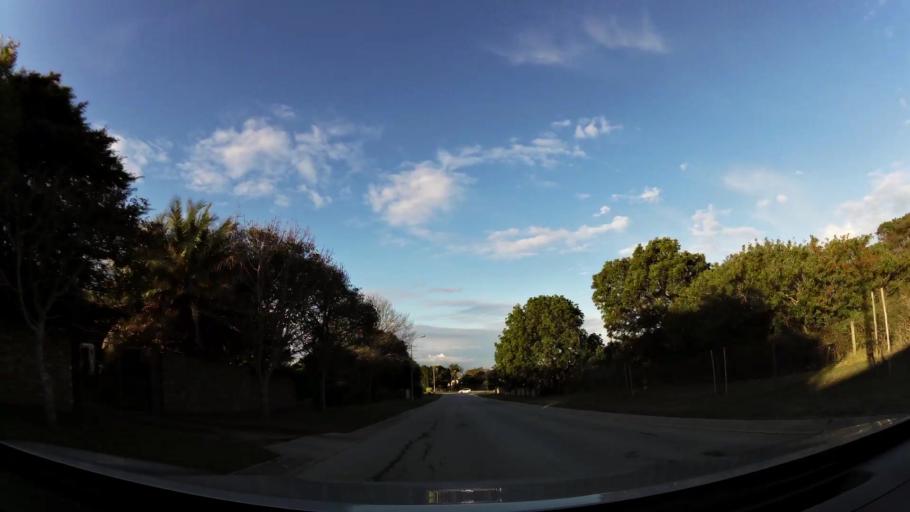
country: ZA
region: Eastern Cape
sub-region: Nelson Mandela Bay Metropolitan Municipality
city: Port Elizabeth
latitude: -33.9732
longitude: 25.4969
